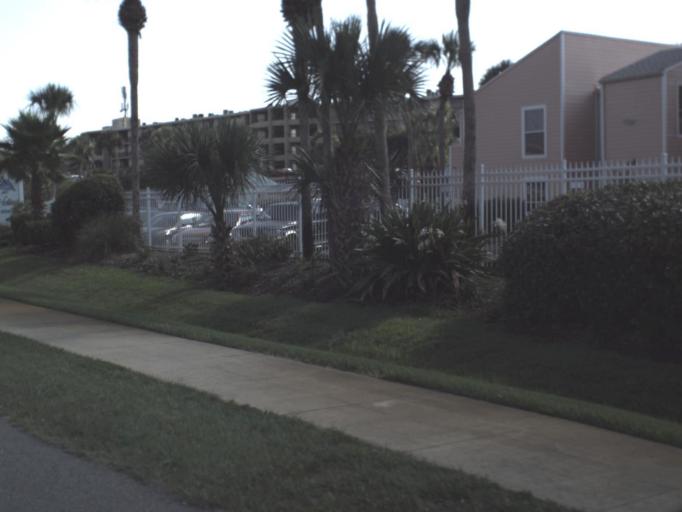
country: US
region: Florida
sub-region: Saint Johns County
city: Butler Beach
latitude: 29.7774
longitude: -81.2569
